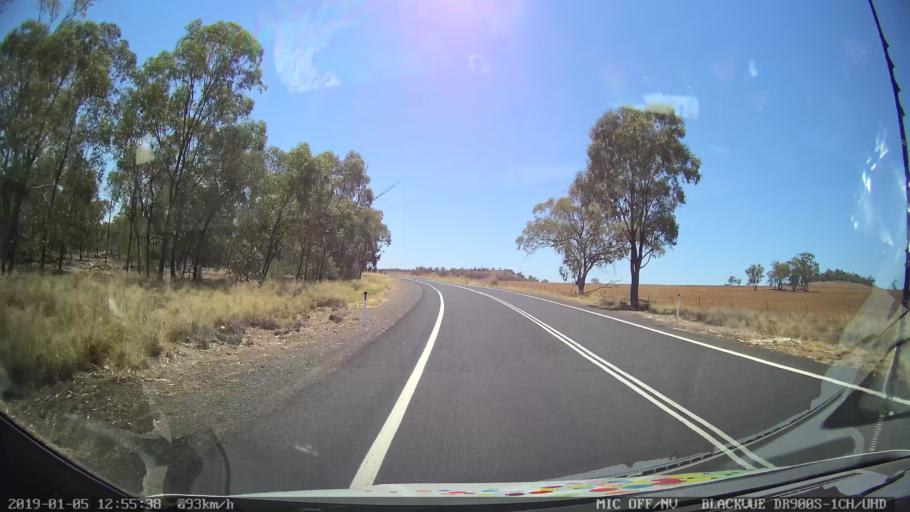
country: AU
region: New South Wales
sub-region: Warrumbungle Shire
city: Coonabarabran
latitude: -31.1199
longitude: 149.7090
